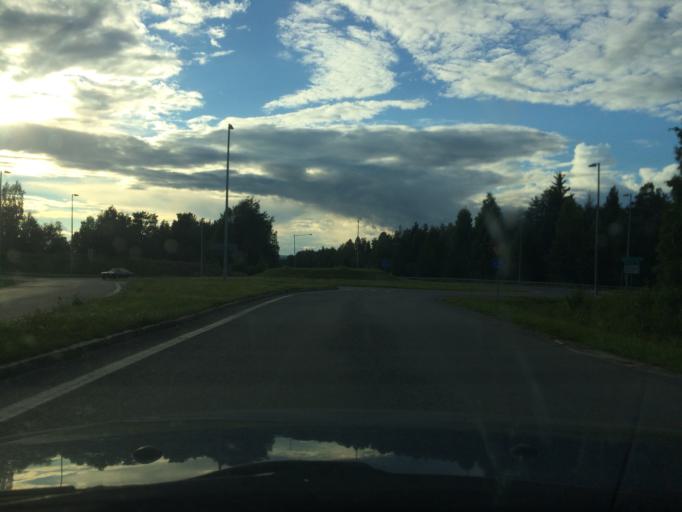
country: SE
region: Norrbotten
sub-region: Pitea Kommun
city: Bergsviken
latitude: 65.3296
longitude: 21.4265
